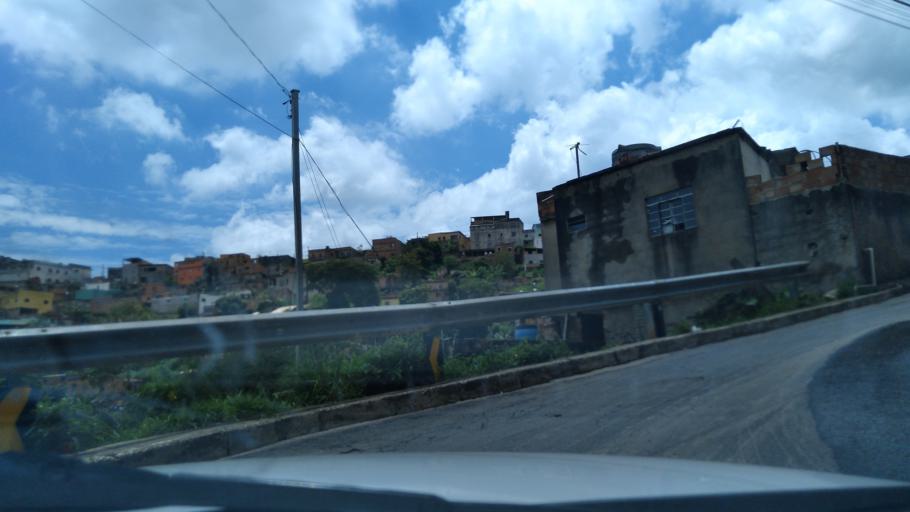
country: BR
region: Minas Gerais
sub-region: Belo Horizonte
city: Belo Horizonte
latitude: -19.9208
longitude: -43.8712
